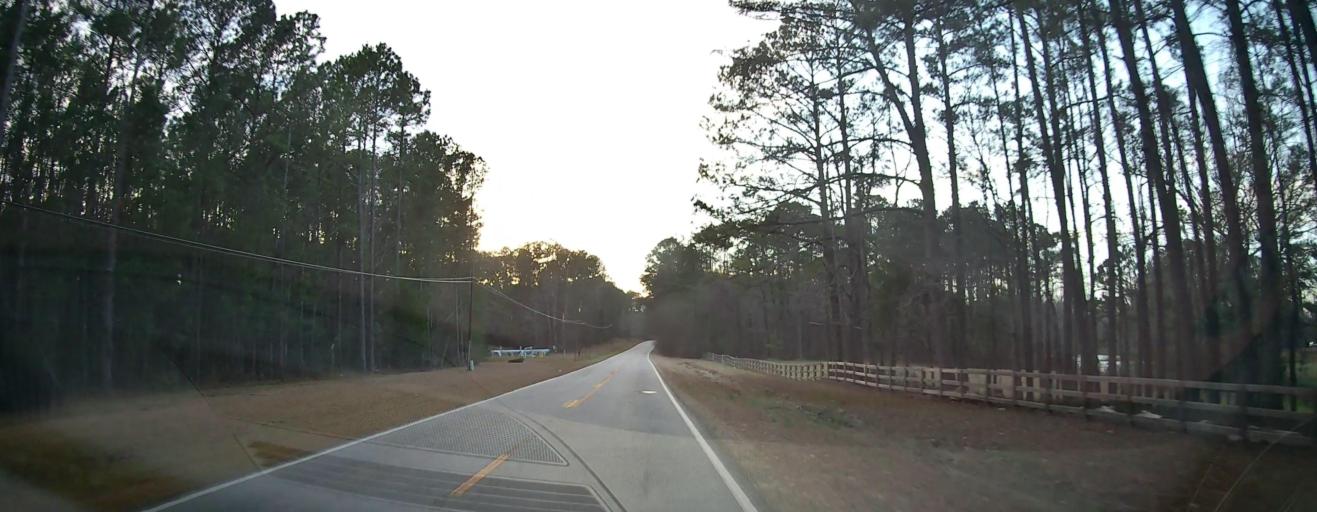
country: US
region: Georgia
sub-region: Harris County
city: Hamilton
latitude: 32.5999
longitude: -84.8832
